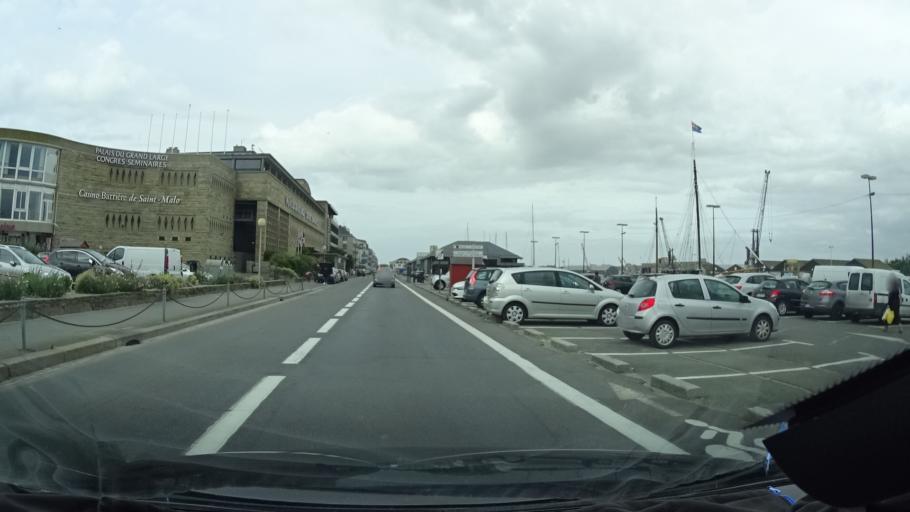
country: FR
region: Brittany
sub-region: Departement d'Ille-et-Vilaine
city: Saint-Malo
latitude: 48.6513
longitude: -2.0205
